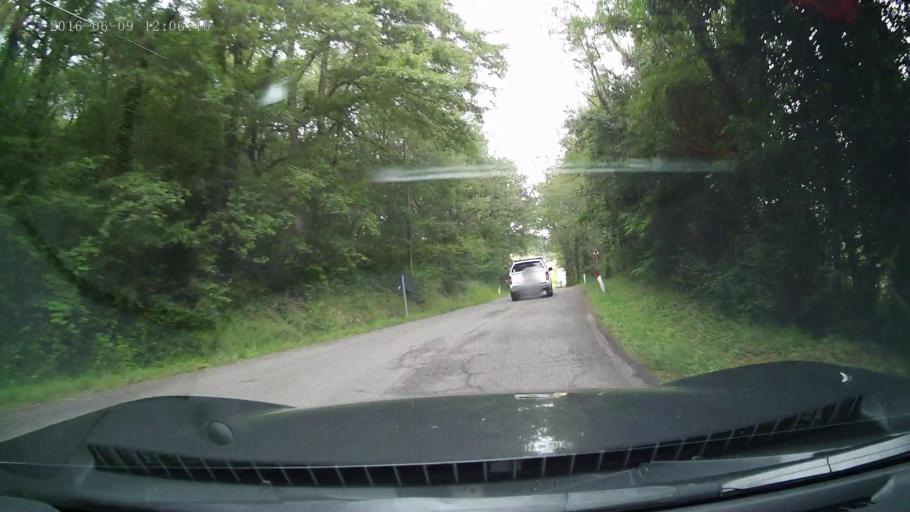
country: IT
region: Tuscany
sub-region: Province of Florence
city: Panzano in Chianti
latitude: 43.5226
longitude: 11.2909
